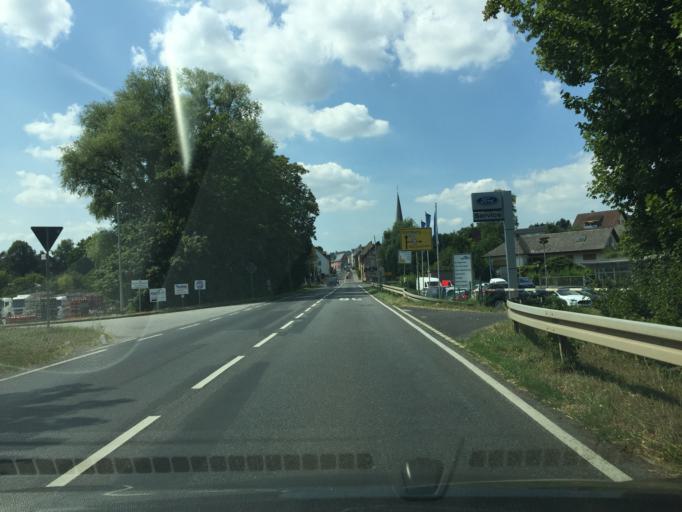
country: DE
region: Hesse
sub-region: Regierungsbezirk Giessen
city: Elz
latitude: 50.4690
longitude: 8.0420
